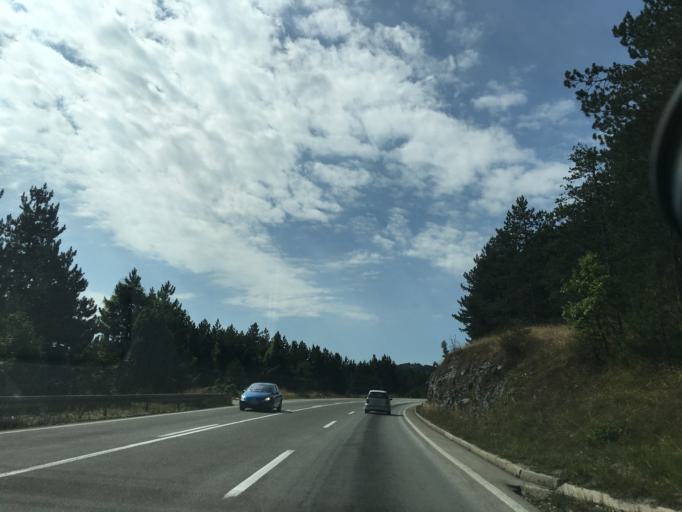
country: RS
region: Central Serbia
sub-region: Zlatiborski Okrug
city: Cajetina
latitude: 43.7593
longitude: 19.7262
